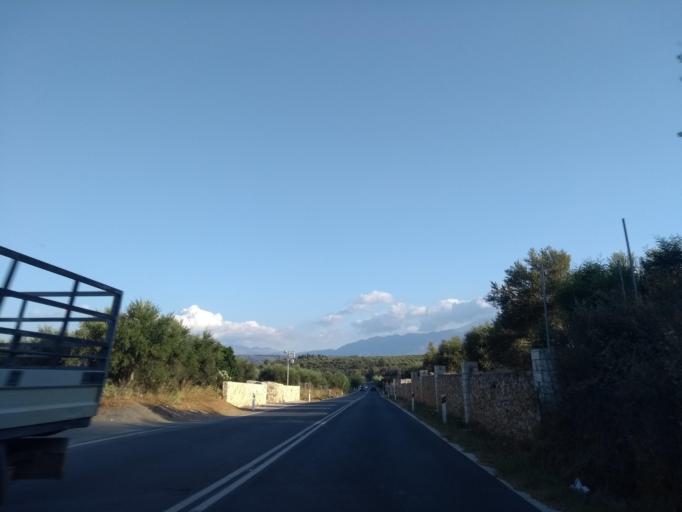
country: GR
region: Crete
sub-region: Nomos Chanias
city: Kalivai
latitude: 35.4639
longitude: 24.1533
